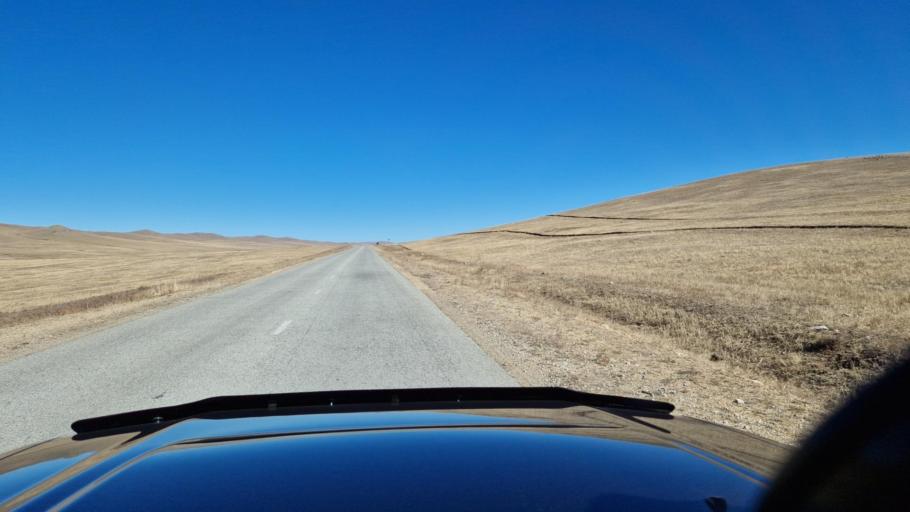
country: MN
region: Hentiy
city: Modot
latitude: 47.7332
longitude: 108.5959
